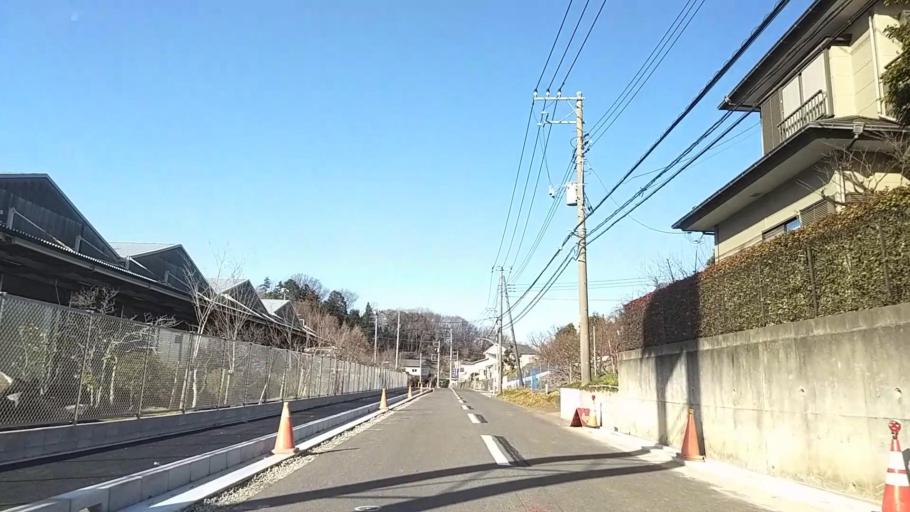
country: JP
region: Kanagawa
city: Atsugi
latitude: 35.4526
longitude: 139.3120
